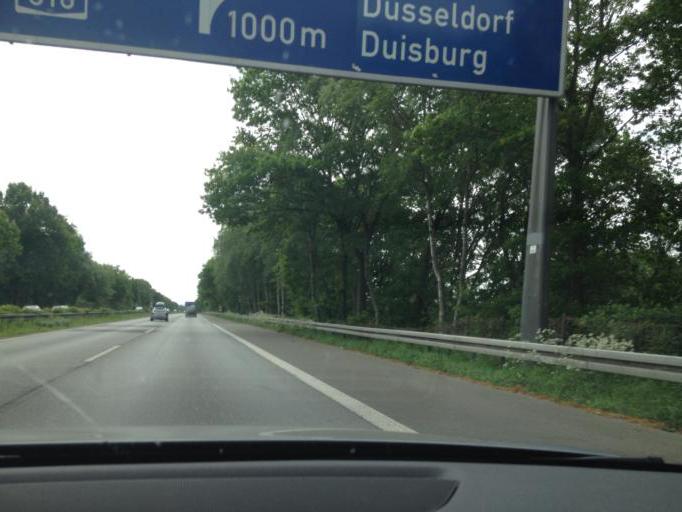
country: DE
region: North Rhine-Westphalia
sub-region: Regierungsbezirk Dusseldorf
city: Dinslaken
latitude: 51.5500
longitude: 6.8173
